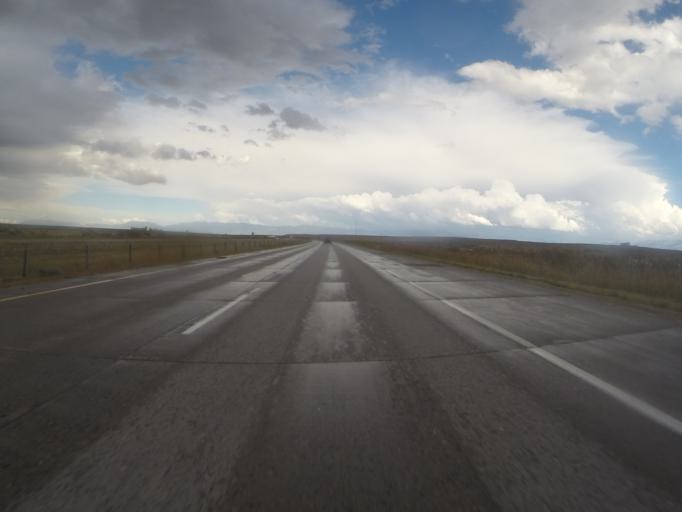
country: US
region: Utah
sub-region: Salt Lake County
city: Magna
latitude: 40.7366
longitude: -112.1953
